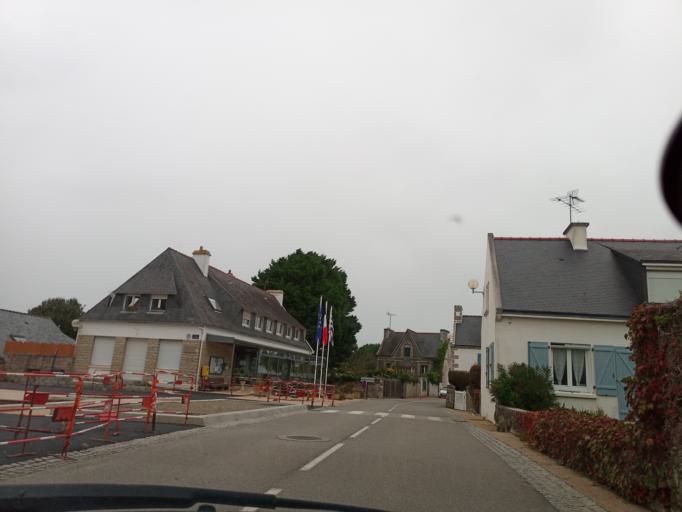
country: FR
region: Brittany
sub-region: Departement du Finistere
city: Esquibien
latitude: 48.0245
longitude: -4.5623
